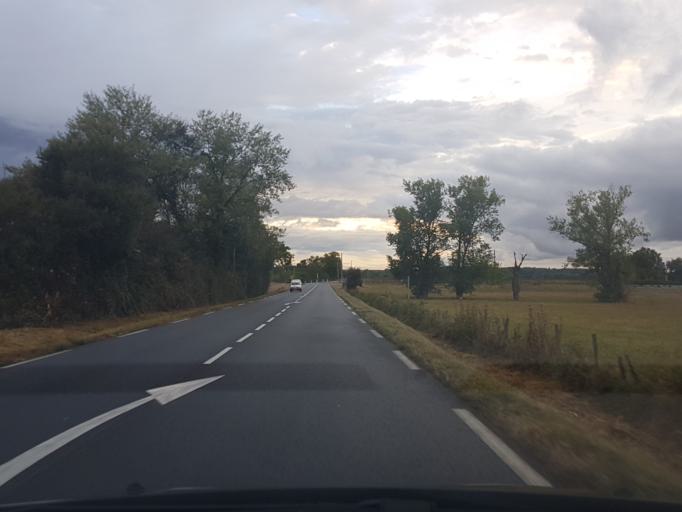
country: FR
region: Midi-Pyrenees
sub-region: Departement de l'Ariege
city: La Tour-du-Crieu
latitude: 43.0889
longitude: 1.7339
